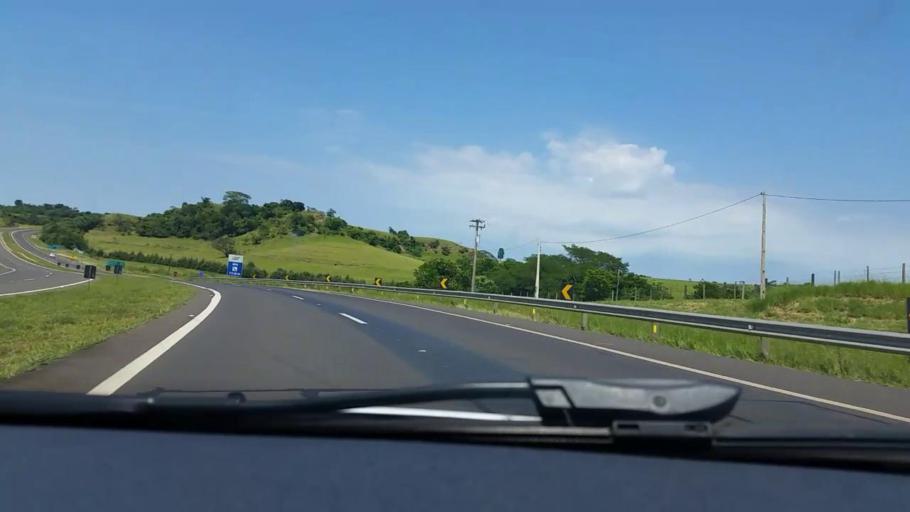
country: BR
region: Sao Paulo
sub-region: Bauru
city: Bauru
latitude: -22.4279
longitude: -49.1312
